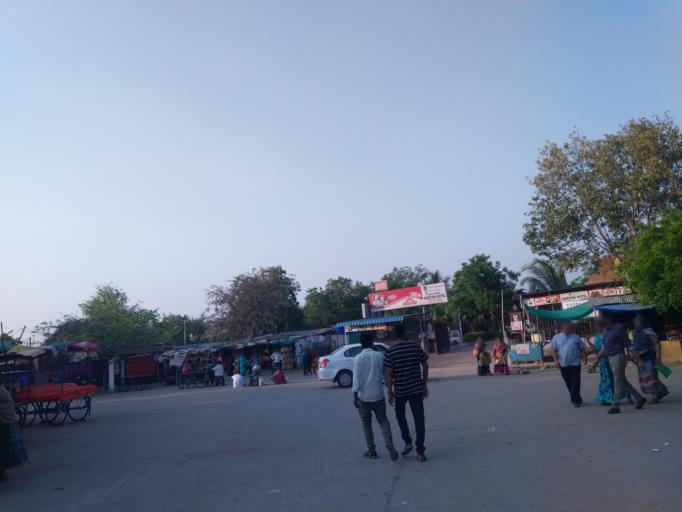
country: IN
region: Telangana
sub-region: Rangareddi
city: Sriramnagar
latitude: 17.3587
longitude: 78.2995
